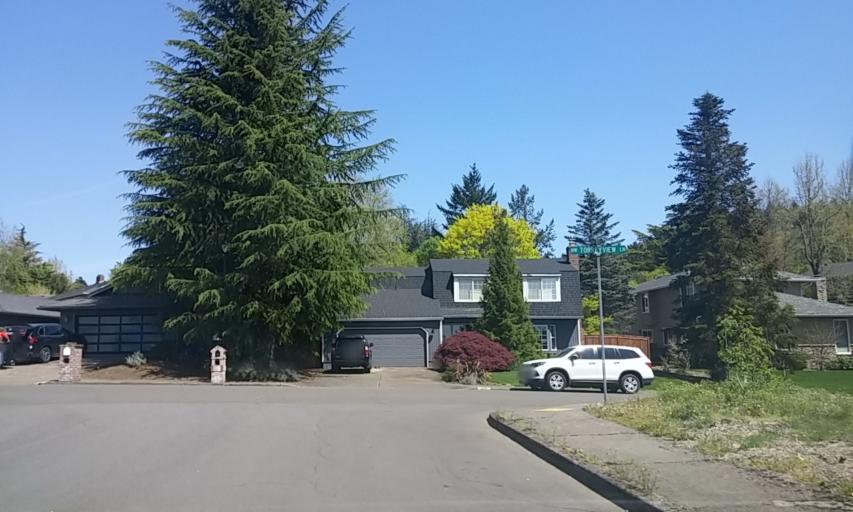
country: US
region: Oregon
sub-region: Washington County
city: West Haven
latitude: 45.5231
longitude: -122.7688
